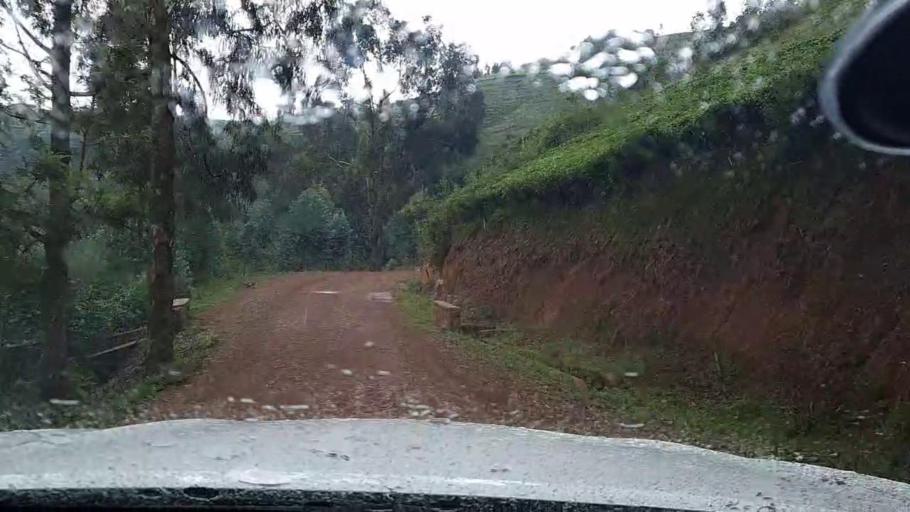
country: RW
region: Western Province
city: Kibuye
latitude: -2.1591
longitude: 29.4346
